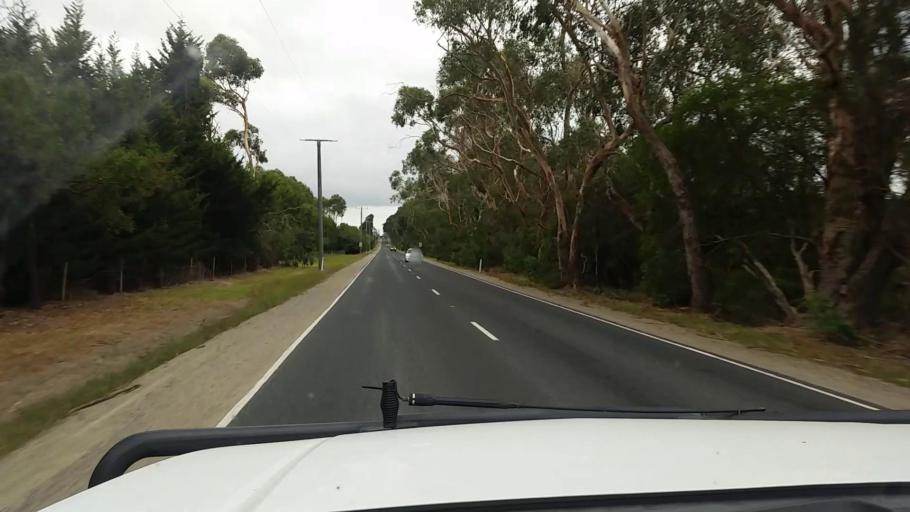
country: AU
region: Victoria
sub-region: Mornington Peninsula
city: Tyabb
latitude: -38.2689
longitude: 145.1456
